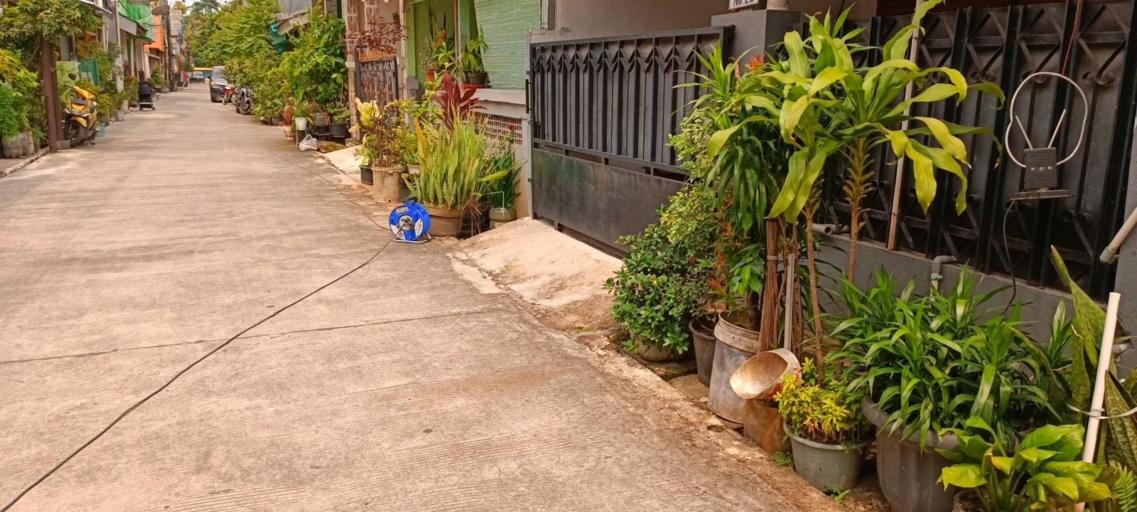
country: ID
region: West Java
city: Pamulang
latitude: -6.3599
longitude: 106.7304
